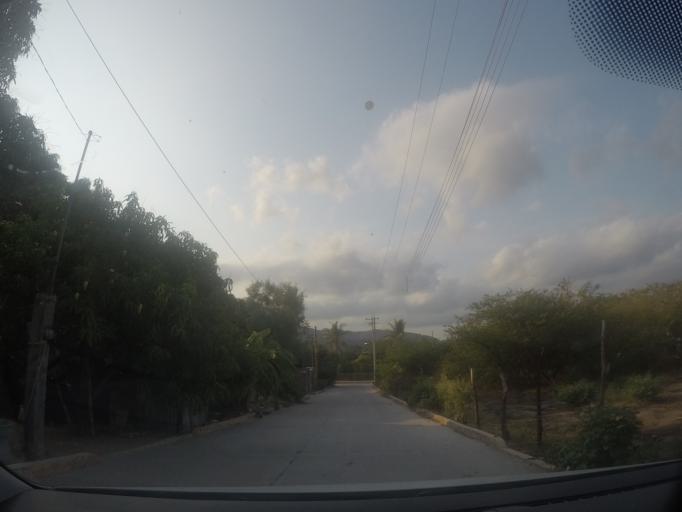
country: MX
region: Oaxaca
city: San Jeronimo Ixtepec
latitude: 16.5818
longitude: -95.1981
